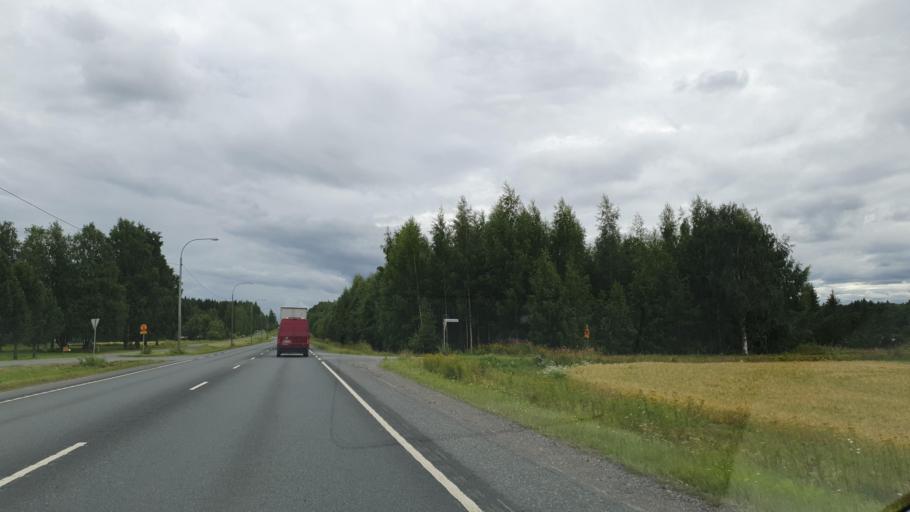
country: FI
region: Northern Savo
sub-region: Ylae-Savo
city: Lapinlahti
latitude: 63.4531
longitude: 27.3178
